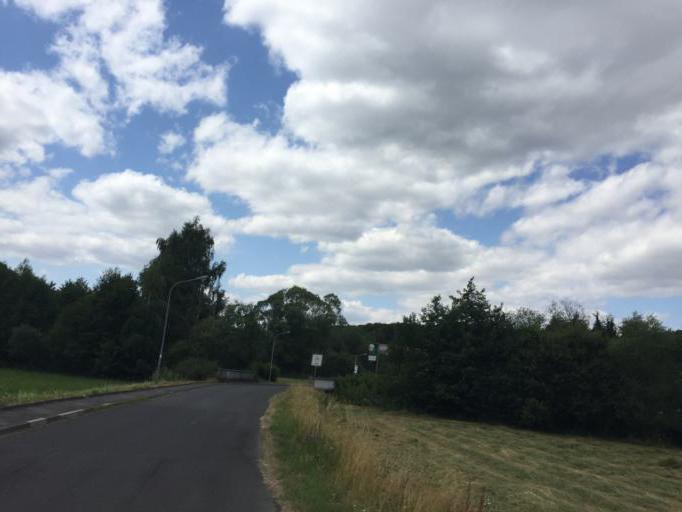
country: DE
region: Hesse
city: Lollar
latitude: 50.6453
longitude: 8.6753
